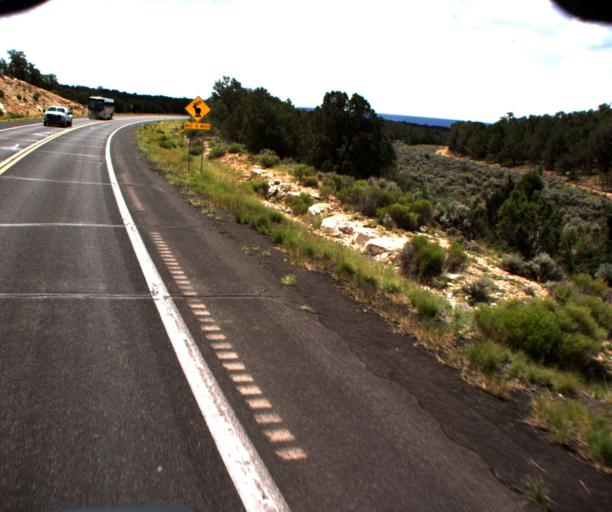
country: US
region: Arizona
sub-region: Coconino County
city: Grand Canyon
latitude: 36.0037
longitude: -111.7996
